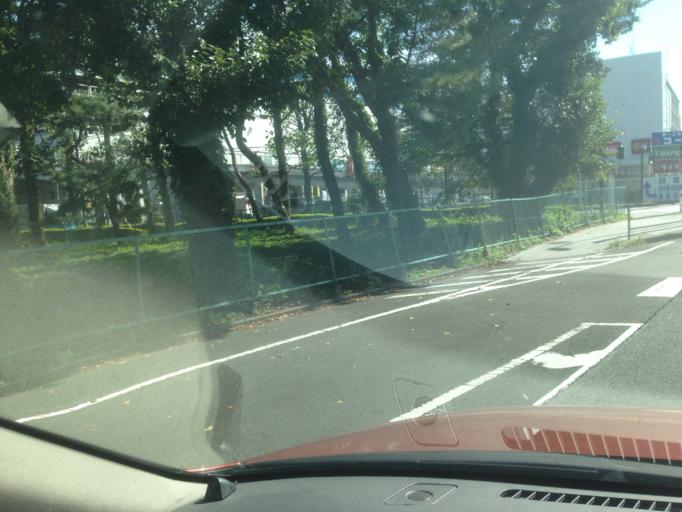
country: JP
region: Tokyo
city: Hachioji
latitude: 35.5830
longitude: 139.3546
